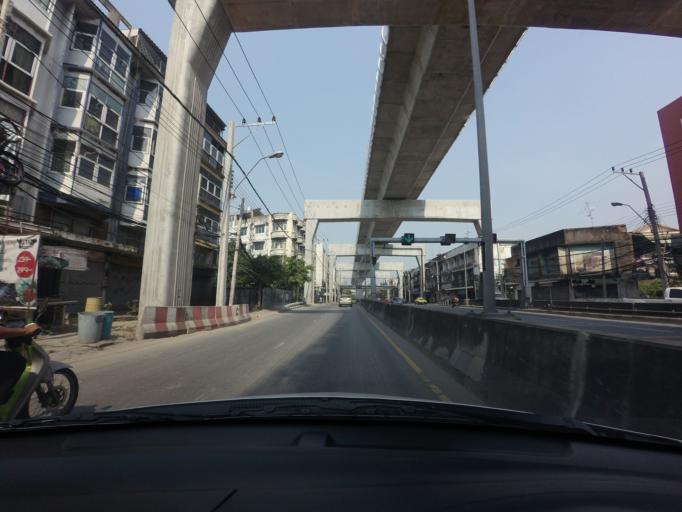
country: TH
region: Bangkok
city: Bangkok Yai
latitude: 13.7324
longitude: 100.4725
